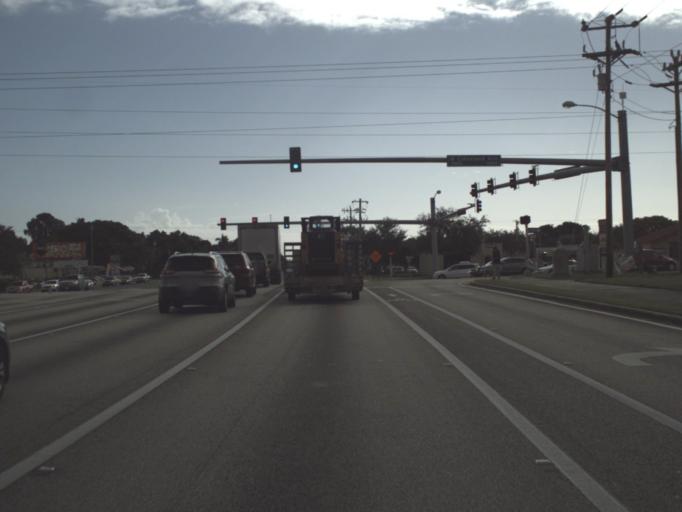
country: US
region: Florida
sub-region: Lee County
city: Palmona Park
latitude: 26.6820
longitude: -81.9023
